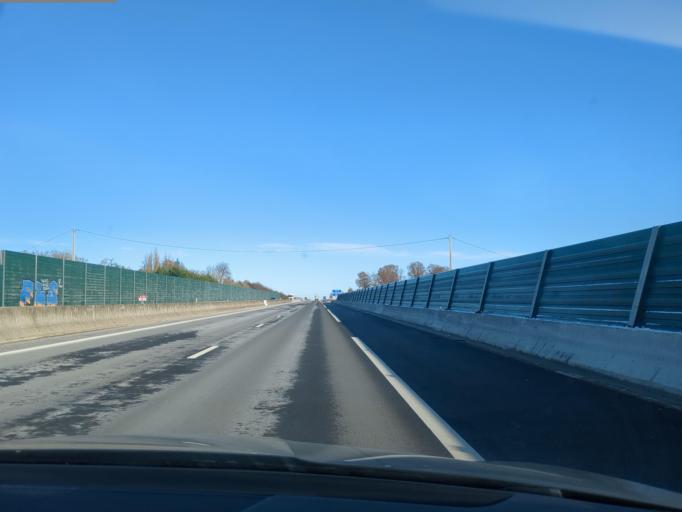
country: FR
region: Auvergne
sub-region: Departement de l'Allier
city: Souvigny
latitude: 46.4266
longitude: 3.1237
